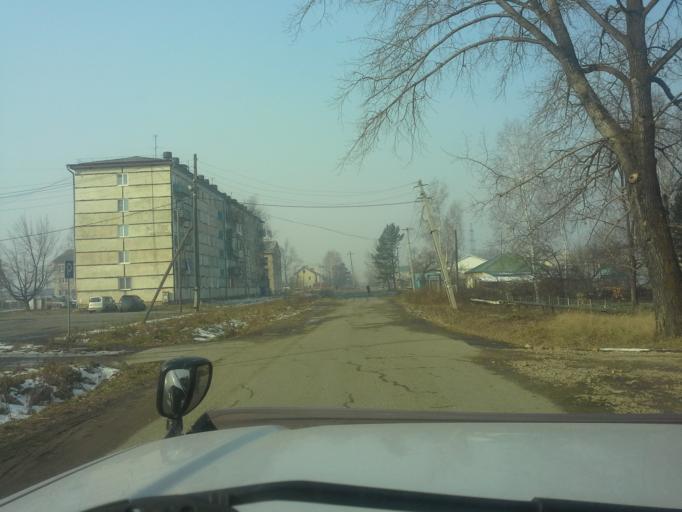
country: RU
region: Jewish Autonomous Oblast
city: Priamurskiy
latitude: 48.5287
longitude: 134.9019
